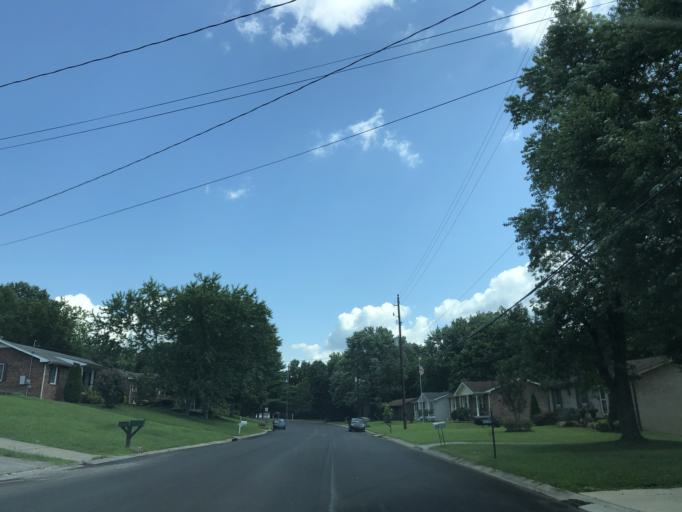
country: US
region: Tennessee
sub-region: Wilson County
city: Green Hill
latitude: 36.2201
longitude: -86.5896
